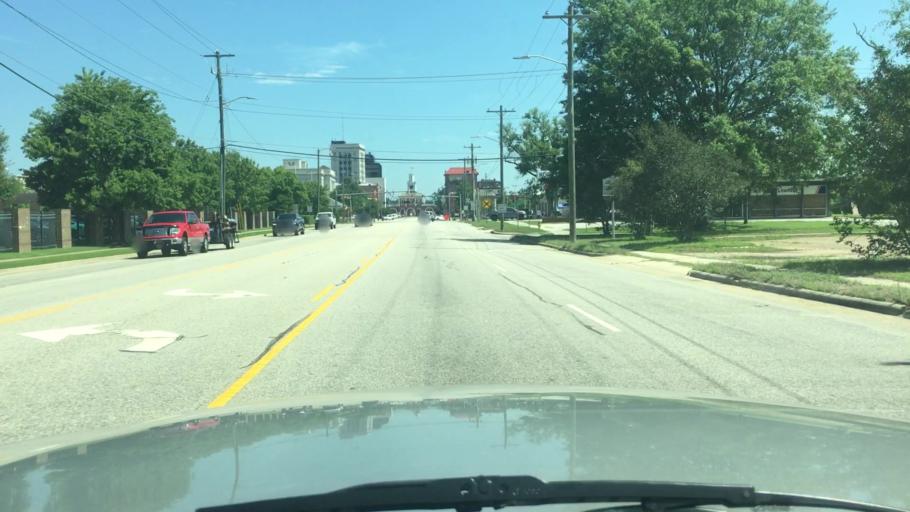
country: US
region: North Carolina
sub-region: Cumberland County
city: Fayetteville
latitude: 35.0487
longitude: -78.8796
